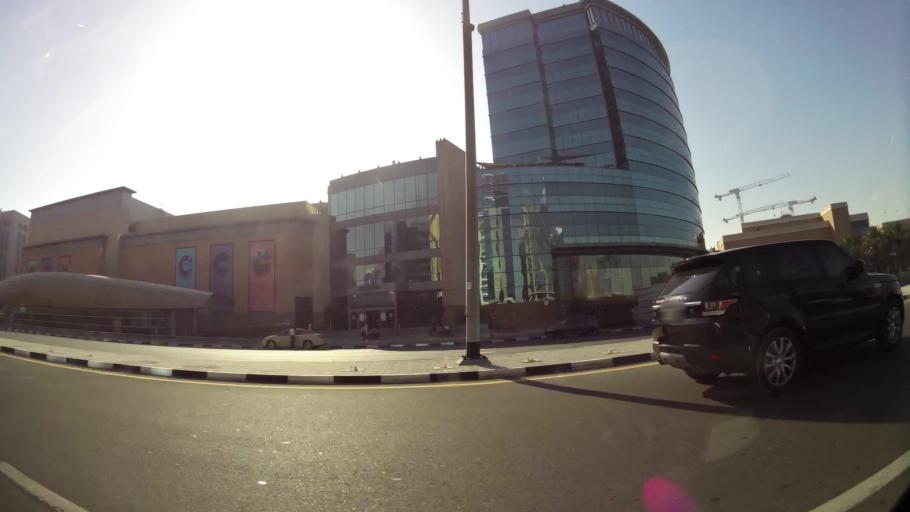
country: AE
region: Ash Shariqah
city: Sharjah
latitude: 25.2533
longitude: 55.3300
